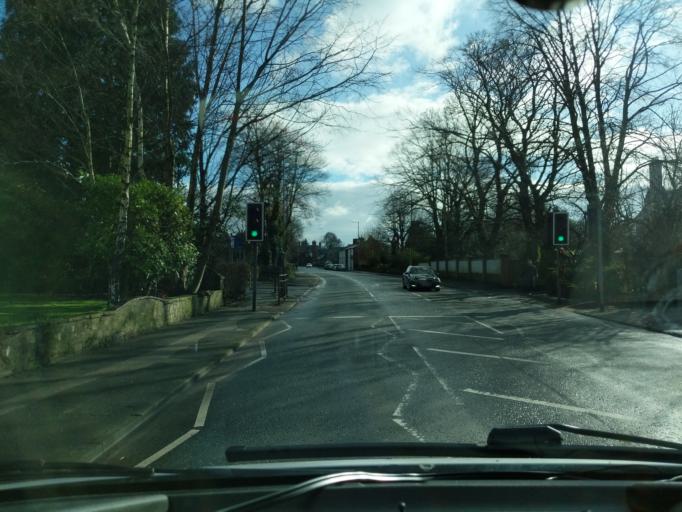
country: GB
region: England
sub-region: St. Helens
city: Eccleston
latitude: 53.4649
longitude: -2.7626
